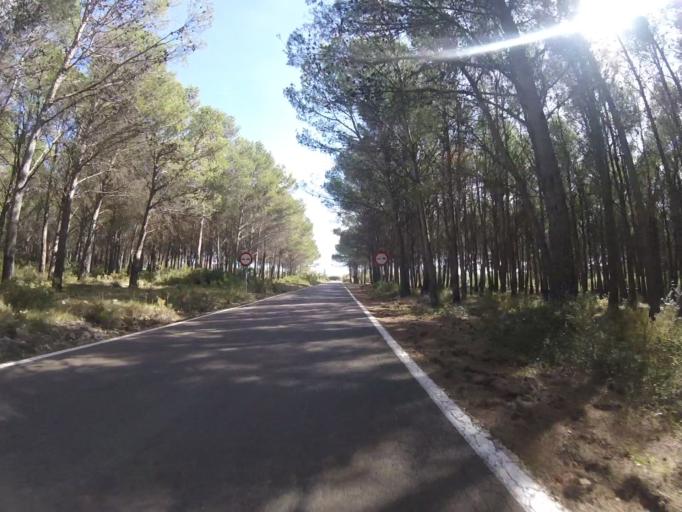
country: ES
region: Valencia
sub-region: Provincia de Castello
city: Albocasser
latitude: 40.4036
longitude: 0.0808
